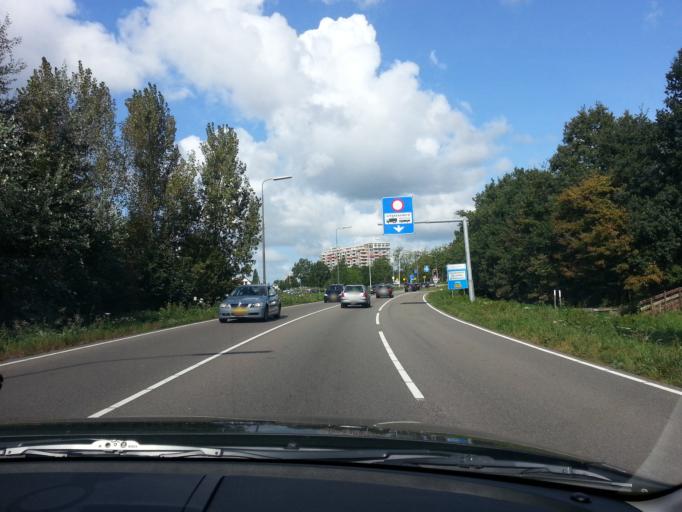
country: NL
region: South Holland
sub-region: Gemeente Leiden
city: Leiden
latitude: 52.1375
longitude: 4.4879
